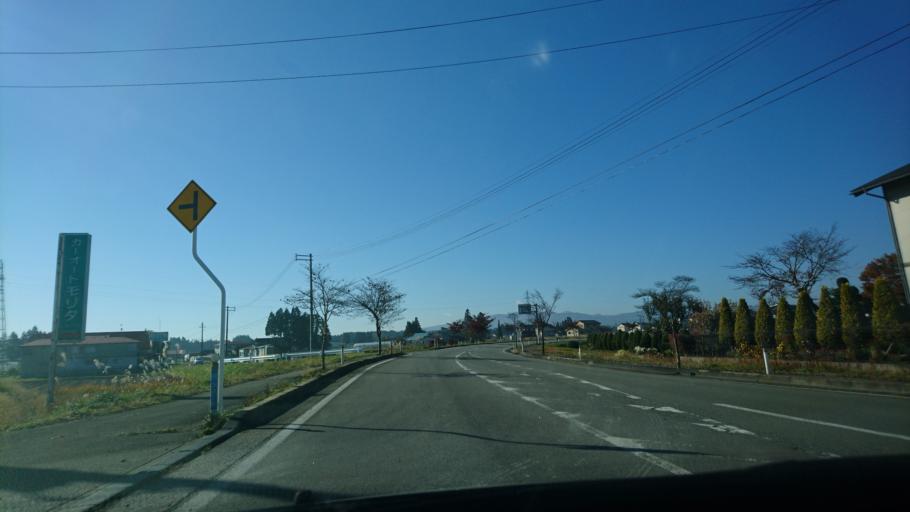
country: JP
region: Iwate
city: Mizusawa
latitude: 39.1307
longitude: 141.0645
